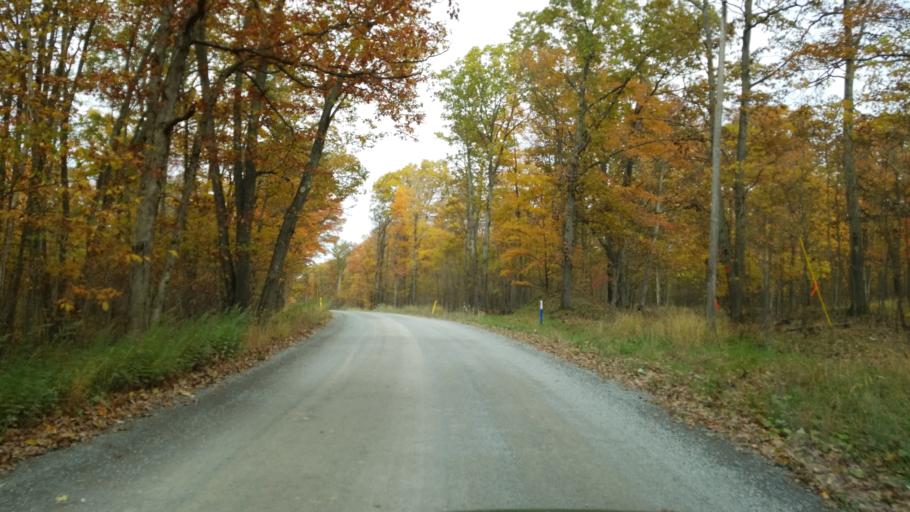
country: US
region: Pennsylvania
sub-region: Clearfield County
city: Clearfield
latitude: 41.1673
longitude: -78.4453
